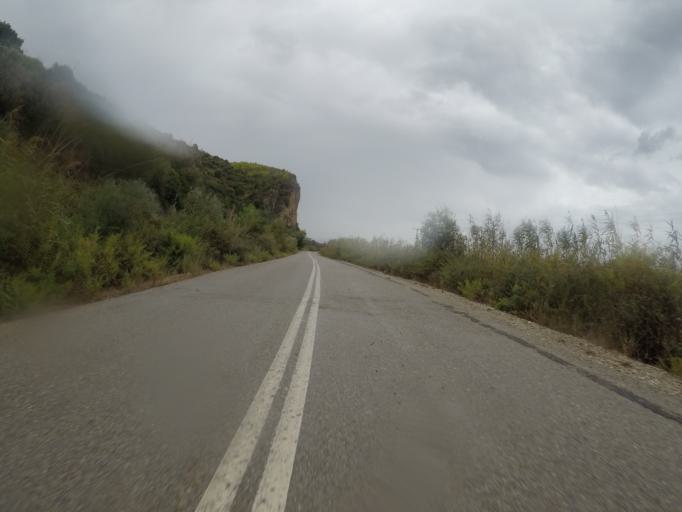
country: GR
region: West Greece
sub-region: Nomos Ileias
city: Zacharo
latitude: 37.5241
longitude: 21.5952
